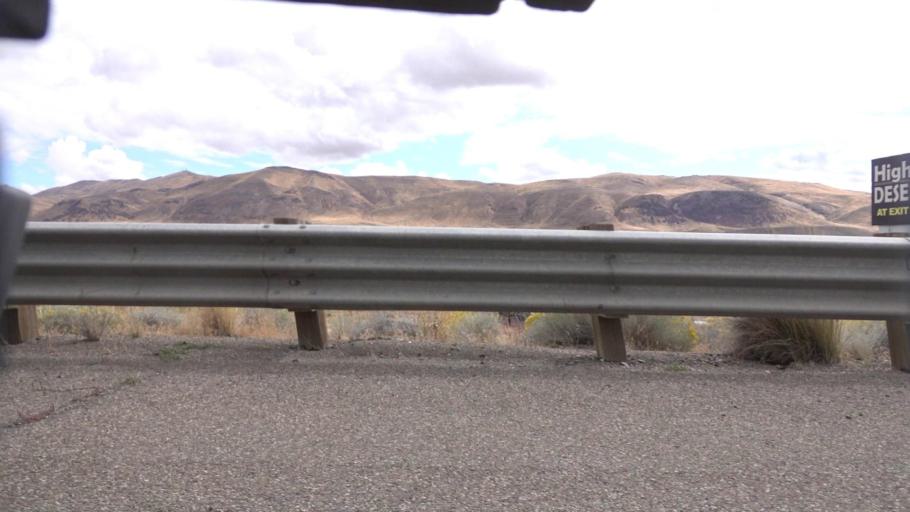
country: US
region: Nevada
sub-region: Elko County
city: Elko
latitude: 40.8915
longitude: -115.7122
